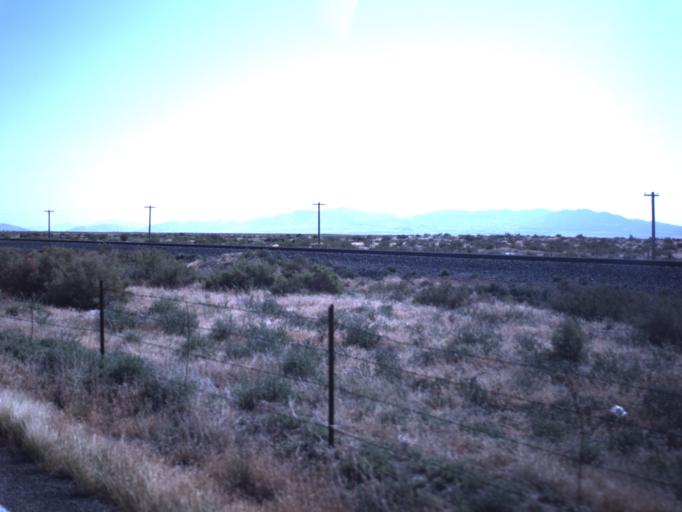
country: US
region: Utah
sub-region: Millard County
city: Delta
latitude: 39.2093
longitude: -112.6823
